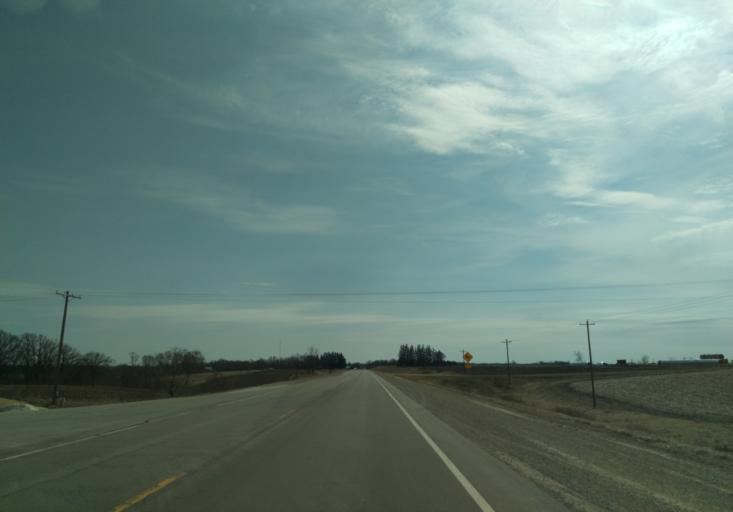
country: US
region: Iowa
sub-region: Winneshiek County
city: Decorah
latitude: 43.4390
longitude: -91.8613
